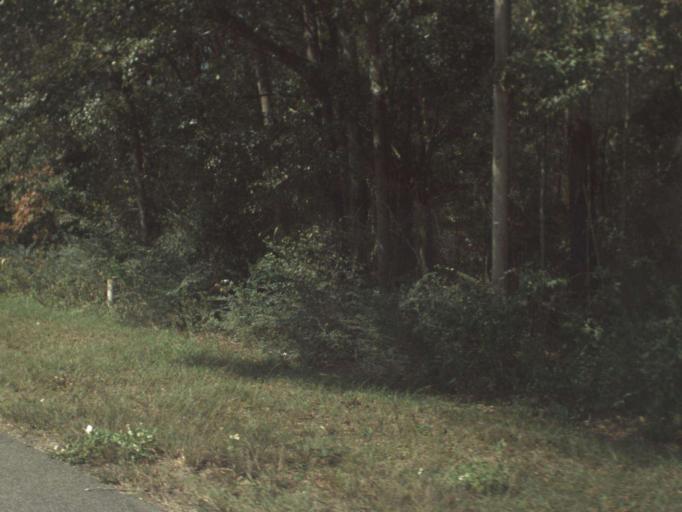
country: US
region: Florida
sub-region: Jackson County
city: Marianna
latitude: 30.7557
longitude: -85.2668
